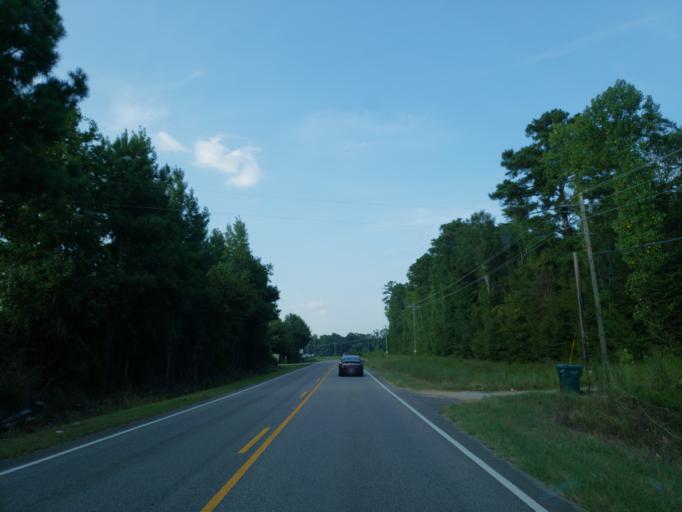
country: US
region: Alabama
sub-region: Hale County
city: Moundville
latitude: 32.9793
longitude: -87.7896
